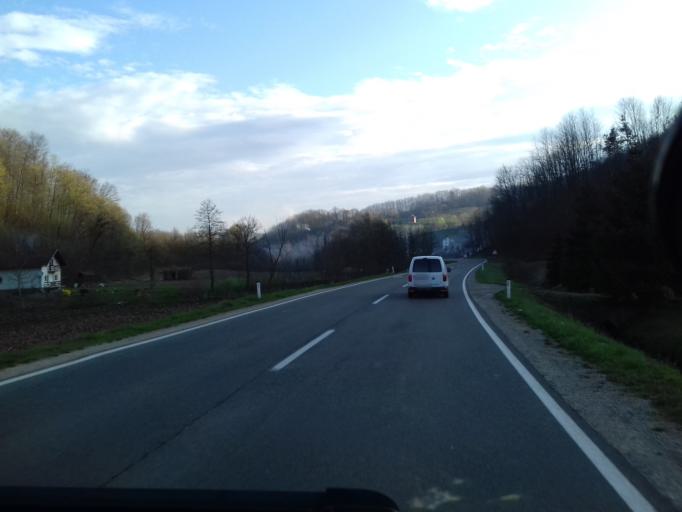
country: BA
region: Federation of Bosnia and Herzegovina
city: Lijesnica
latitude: 44.5050
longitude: 18.0802
